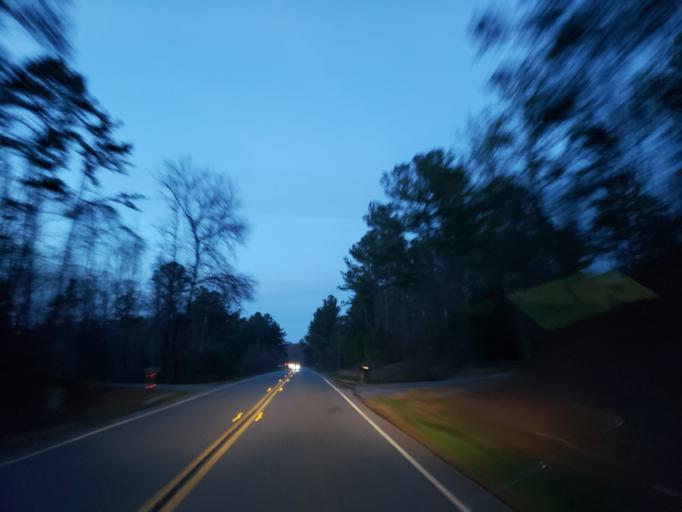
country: US
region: Georgia
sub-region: Cherokee County
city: Ball Ground
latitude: 34.3098
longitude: -84.2698
